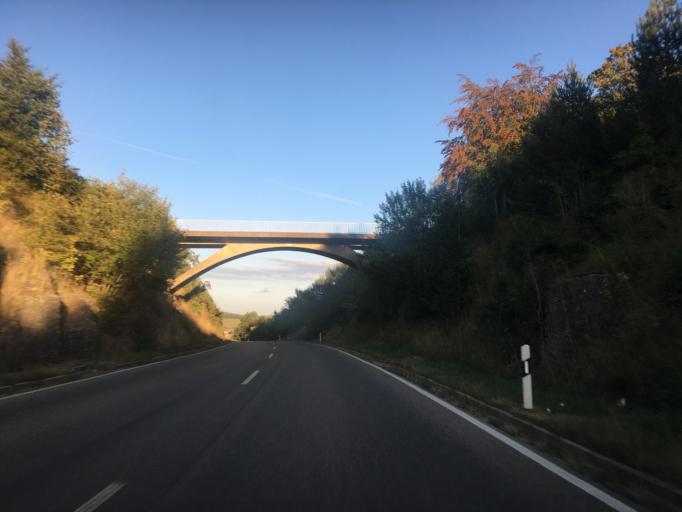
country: DE
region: Baden-Wuerttemberg
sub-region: Tuebingen Region
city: Pfullingen
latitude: 48.3977
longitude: 9.2669
